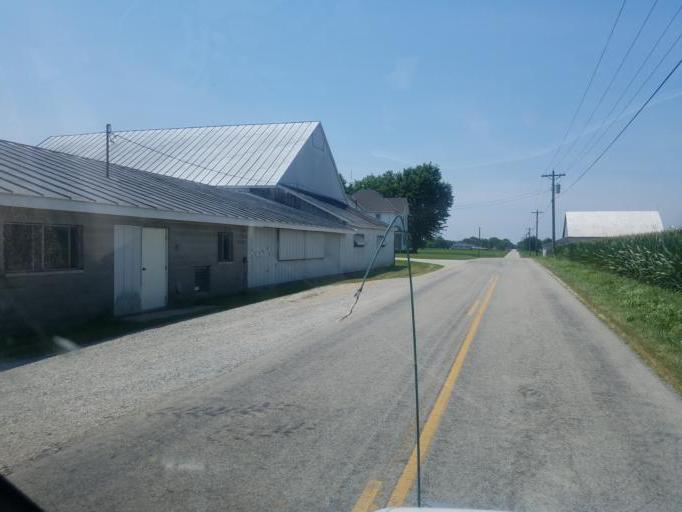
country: US
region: Ohio
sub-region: Shelby County
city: Fort Loramie
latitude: 40.3291
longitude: -84.3557
